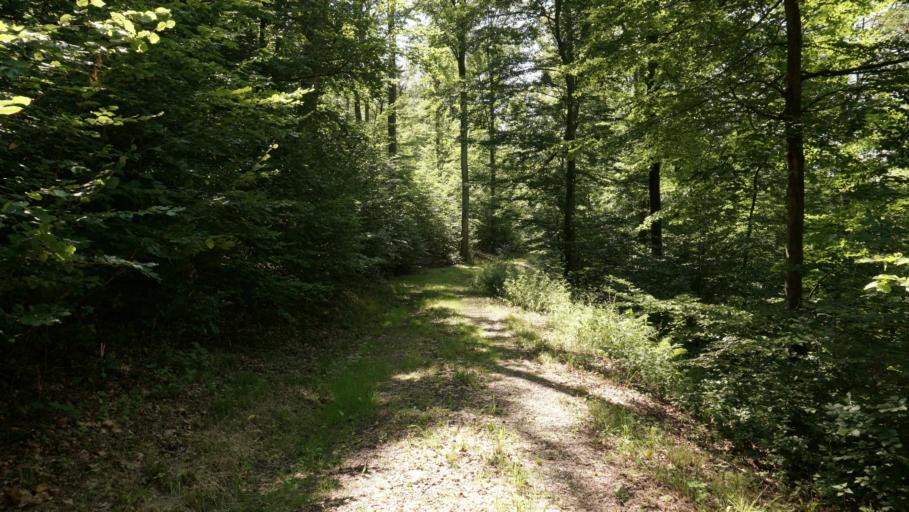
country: DE
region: Baden-Wuerttemberg
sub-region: Karlsruhe Region
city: Neckarzimmern
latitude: 49.3297
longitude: 9.1516
